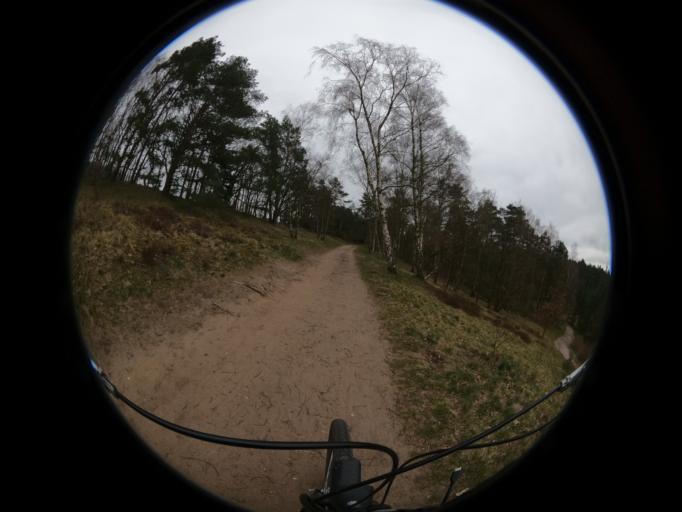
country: DE
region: Lower Saxony
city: Neu Wulmstorf
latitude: 53.4636
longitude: 9.8459
